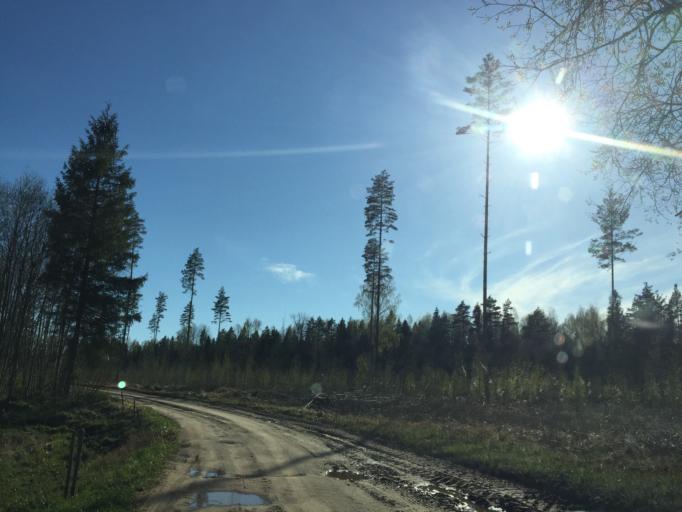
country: EE
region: Valgamaa
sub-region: Valga linn
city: Valga
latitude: 57.7801
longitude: 26.2336
